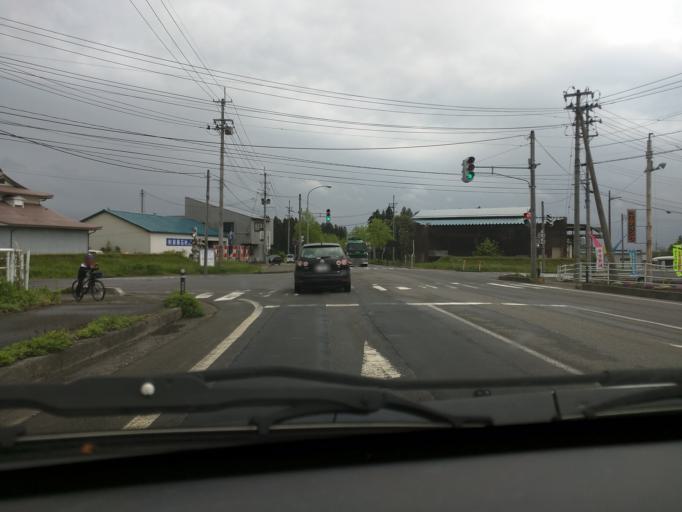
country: JP
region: Fukushima
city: Kitakata
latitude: 37.6713
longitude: 139.8892
